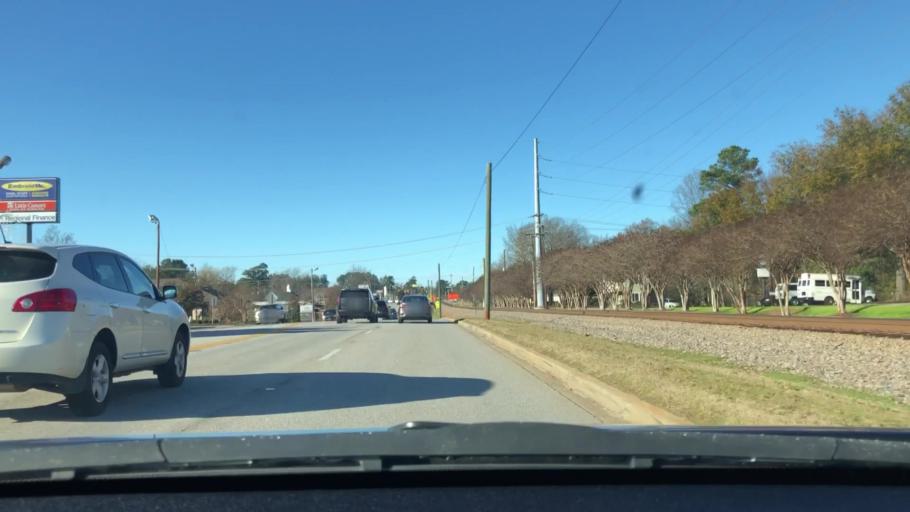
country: US
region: South Carolina
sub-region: Lexington County
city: Irmo
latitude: 34.0821
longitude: -81.1812
